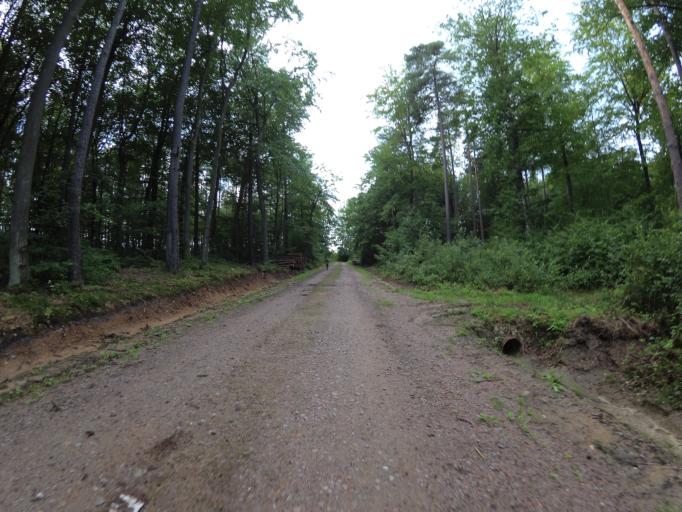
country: PL
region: Pomeranian Voivodeship
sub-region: Powiat wejherowski
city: Bojano
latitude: 54.5075
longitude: 18.4167
